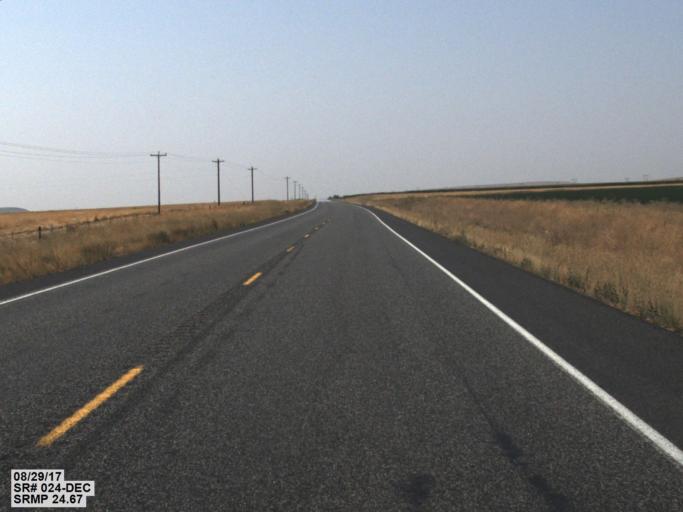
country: US
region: Washington
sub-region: Grant County
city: Desert Aire
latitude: 46.5198
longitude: -119.9964
